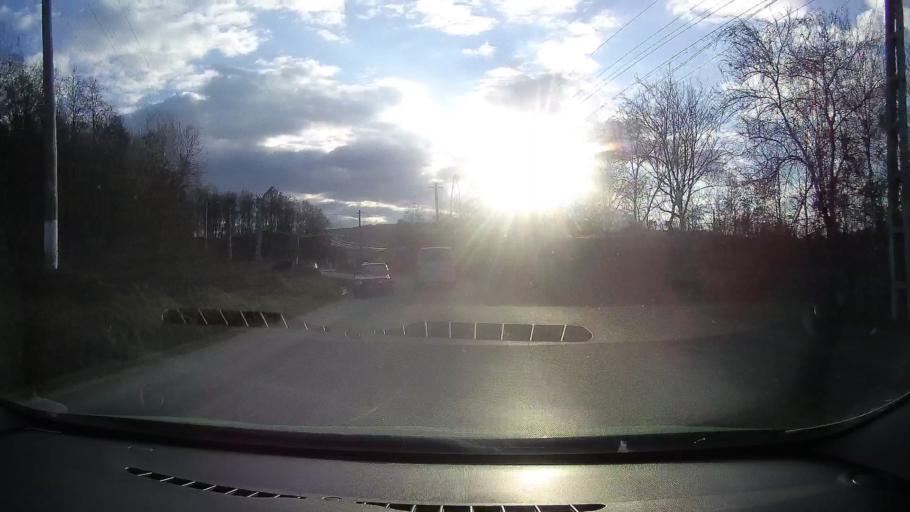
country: RO
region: Dambovita
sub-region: Comuna Ocnita
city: Ocnita
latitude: 44.9706
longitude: 25.5497
